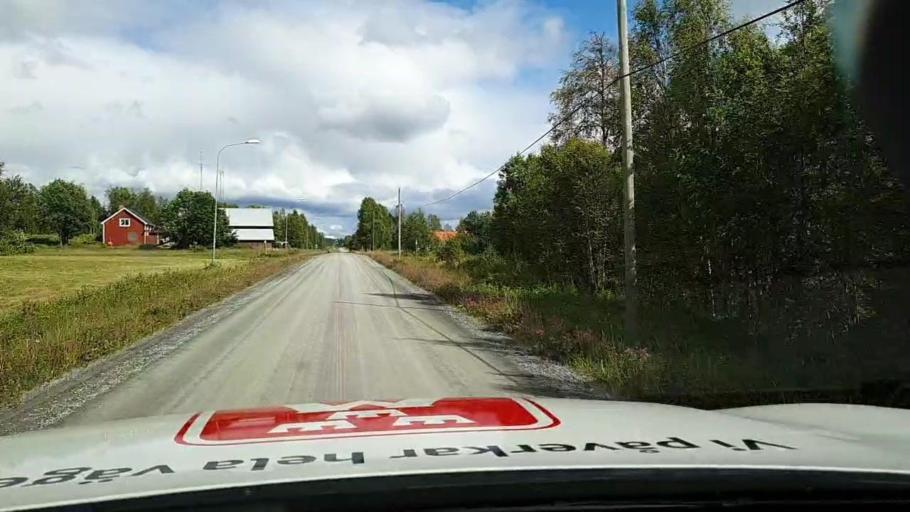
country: SE
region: Jaemtland
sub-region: Krokoms Kommun
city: Valla
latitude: 63.6967
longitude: 13.6276
